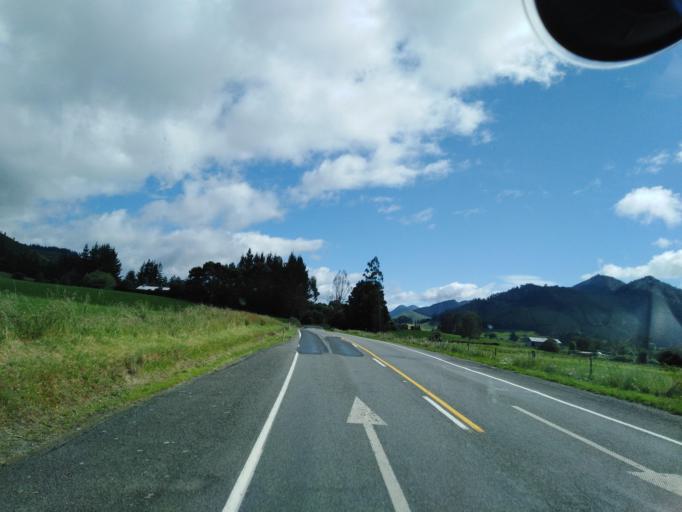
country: NZ
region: Nelson
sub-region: Nelson City
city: Nelson
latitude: -41.2825
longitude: 173.5731
